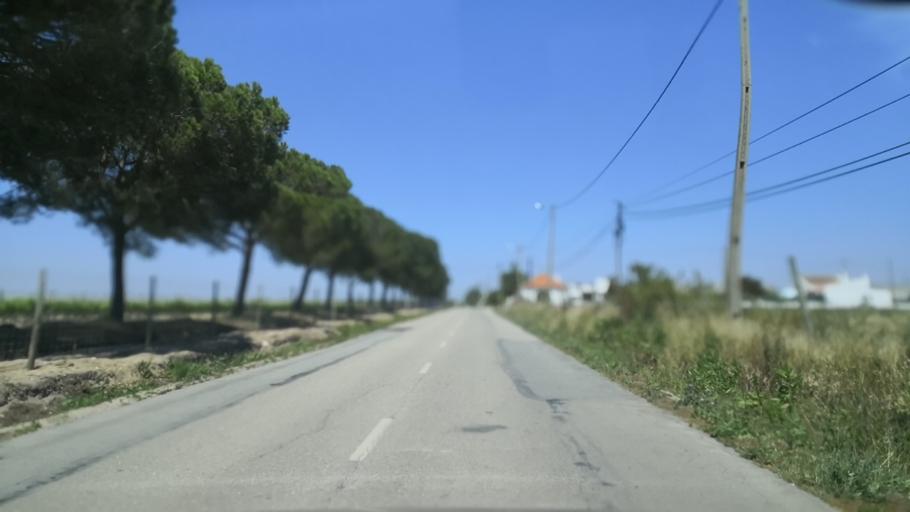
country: PT
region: Santarem
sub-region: Benavente
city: Poceirao
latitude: 38.6790
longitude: -8.7331
